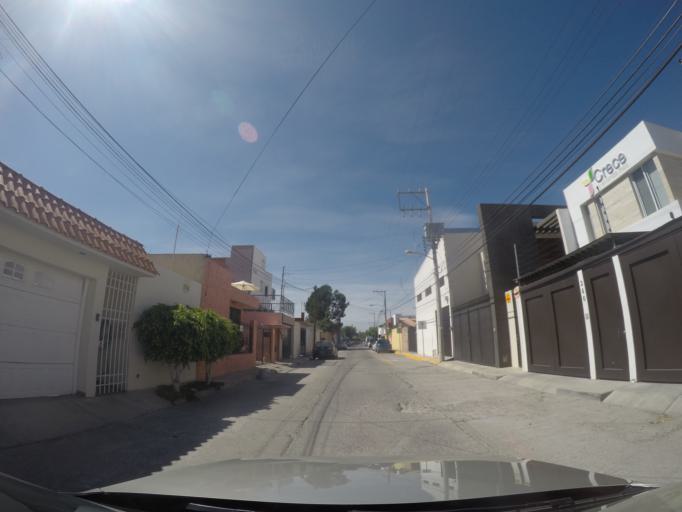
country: MX
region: San Luis Potosi
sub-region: San Luis Potosi
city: San Luis Potosi
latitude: 22.1516
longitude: -101.0082
